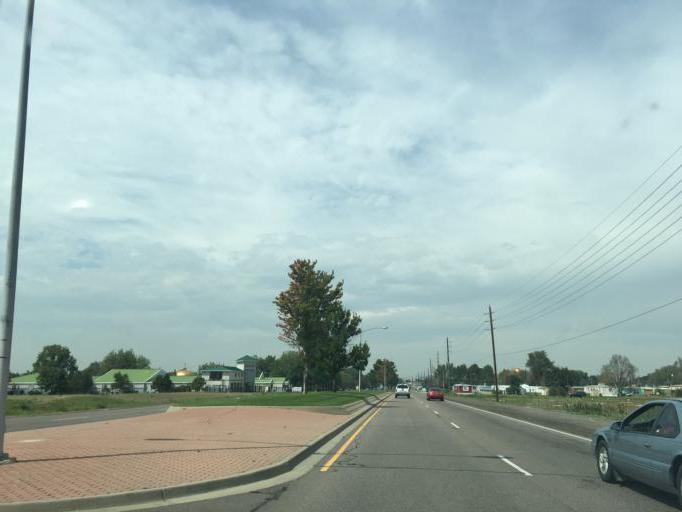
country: US
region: Colorado
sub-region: Adams County
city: Aurora
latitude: 39.7401
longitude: -104.7938
